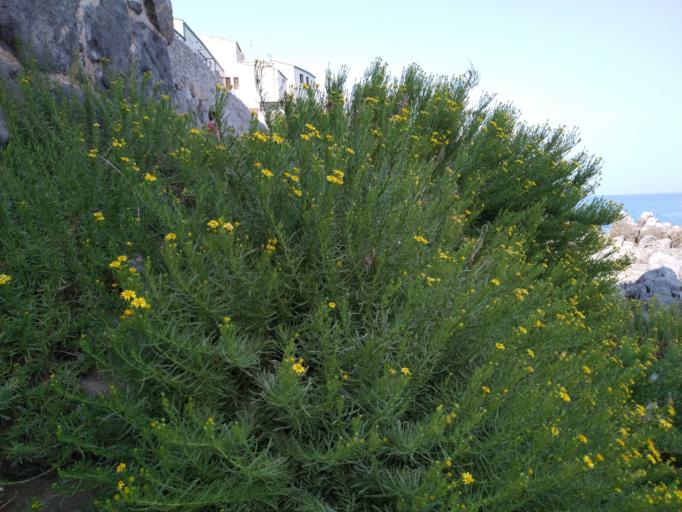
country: IT
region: Sicily
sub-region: Palermo
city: Cefalu
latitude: 38.0408
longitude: 14.0241
